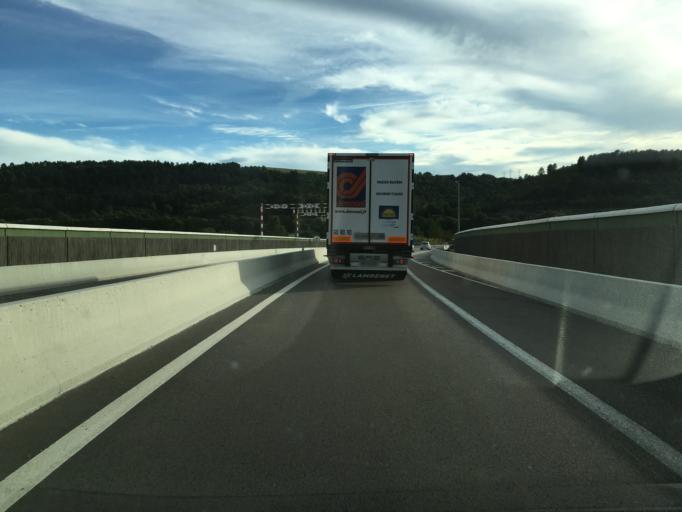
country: FR
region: Bourgogne
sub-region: Departement de la Cote-d'Or
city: Plombieres-les-Dijon
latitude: 47.3354
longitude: 4.9837
